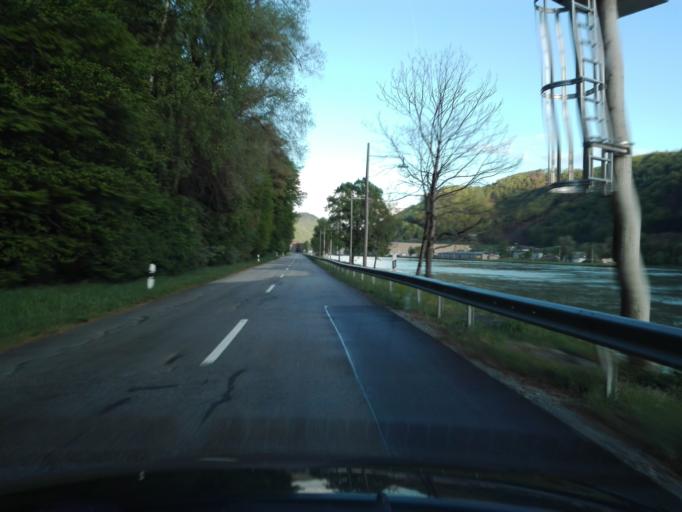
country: DE
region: Bavaria
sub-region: Lower Bavaria
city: Untergriesbach
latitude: 48.5235
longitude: 13.6998
